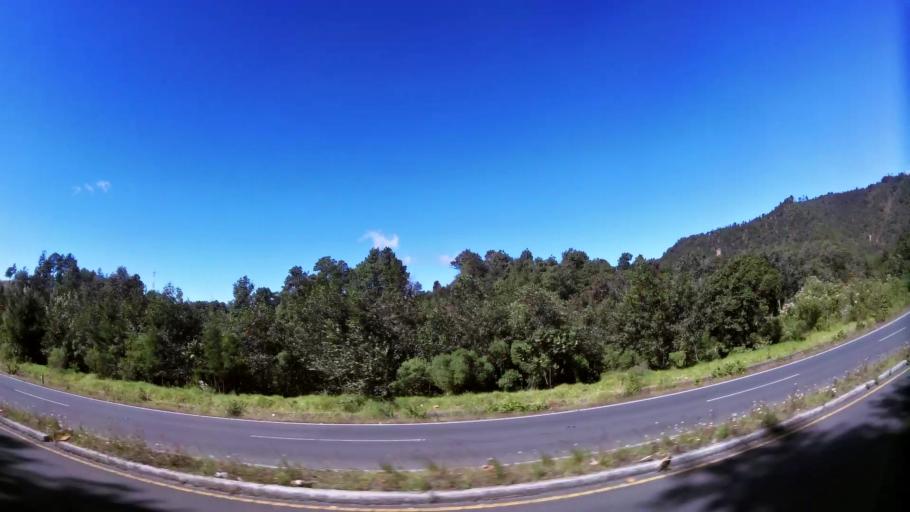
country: GT
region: Solola
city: Solola
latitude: 14.8162
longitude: -91.2013
